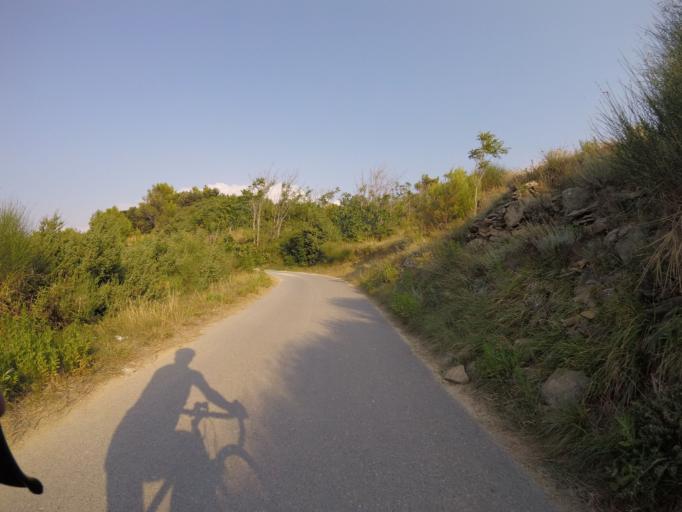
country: HR
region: Primorsko-Goranska
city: Lopar
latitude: 44.8396
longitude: 14.7317
